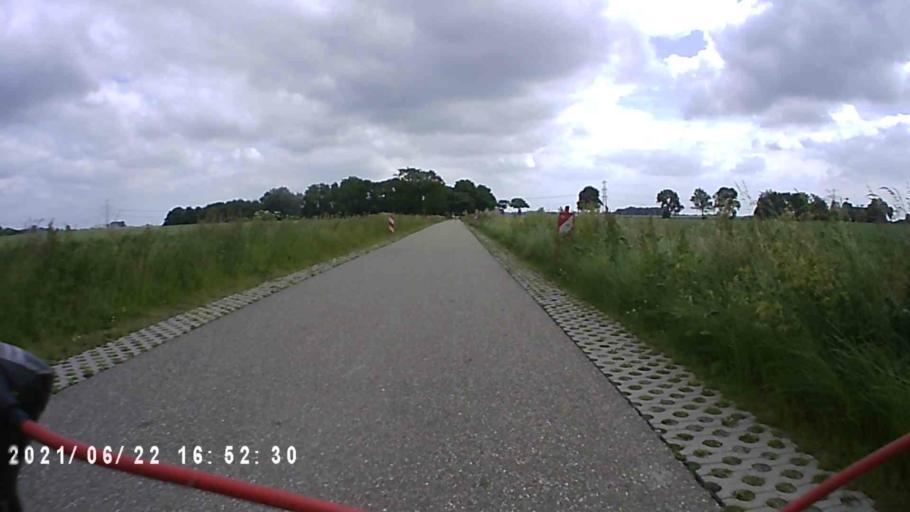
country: NL
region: Groningen
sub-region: Gemeente Bedum
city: Bedum
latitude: 53.3248
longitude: 6.6395
